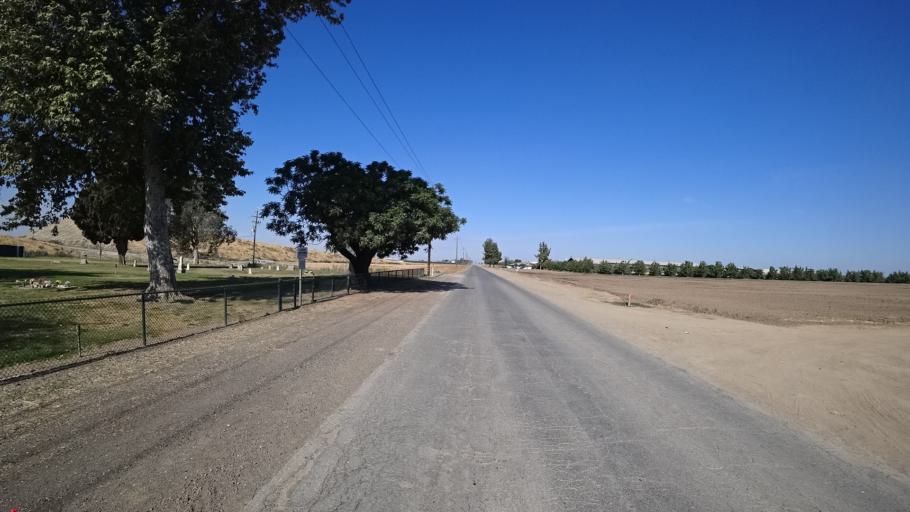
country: US
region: California
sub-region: Kings County
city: Home Garden
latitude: 36.2259
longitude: -119.6074
